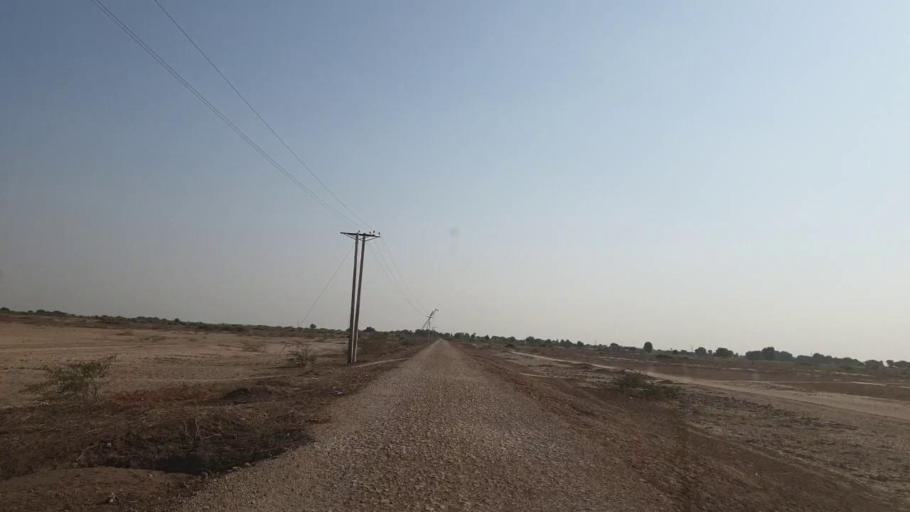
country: PK
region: Sindh
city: Naukot
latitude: 25.0177
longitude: 69.4746
